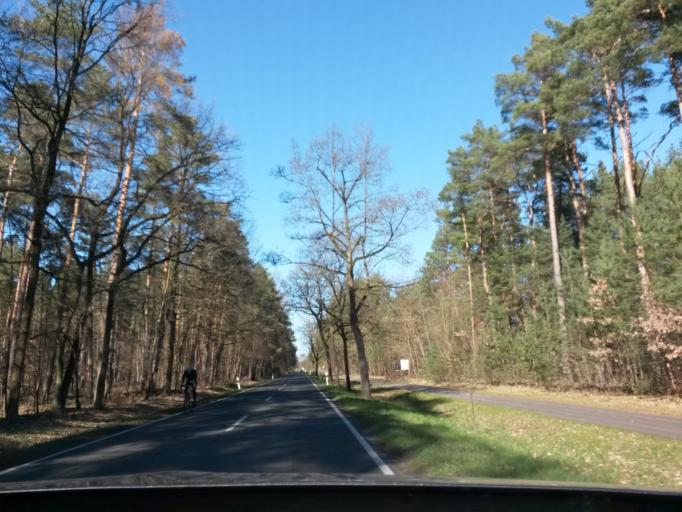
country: DE
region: Brandenburg
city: Rehfelde
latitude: 52.4725
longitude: 13.9082
